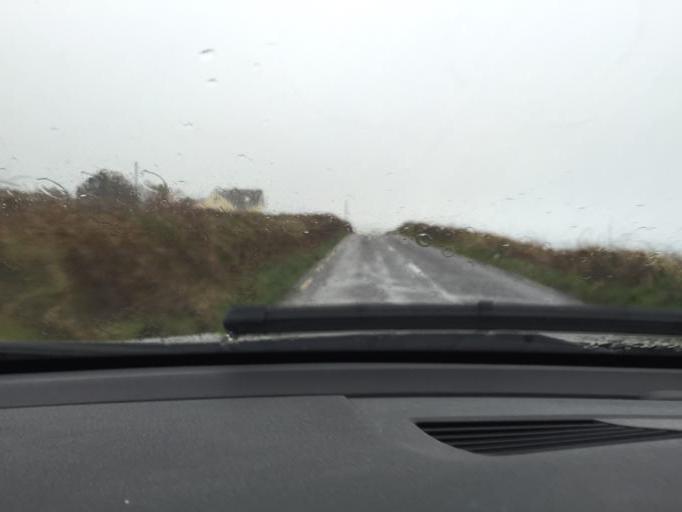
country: IE
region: Munster
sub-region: Ciarrai
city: Dingle
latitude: 52.1276
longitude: -10.3414
